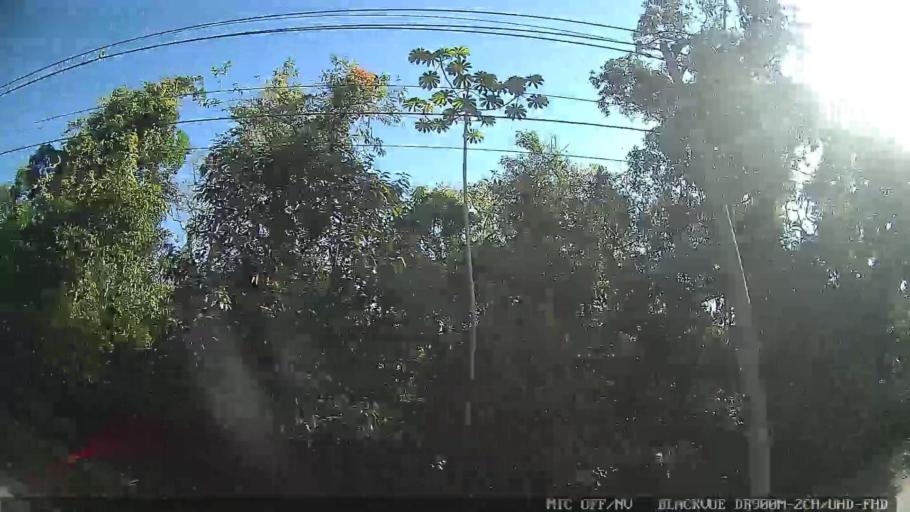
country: BR
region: Sao Paulo
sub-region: Santos
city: Santos
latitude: -23.9023
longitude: -46.3060
